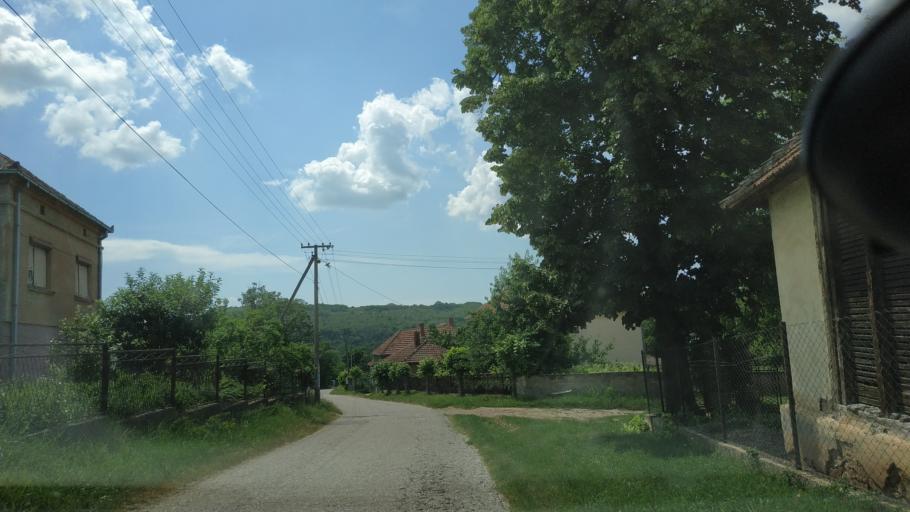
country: RS
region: Central Serbia
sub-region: Nisavski Okrug
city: Aleksinac
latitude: 43.5997
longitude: 21.6894
